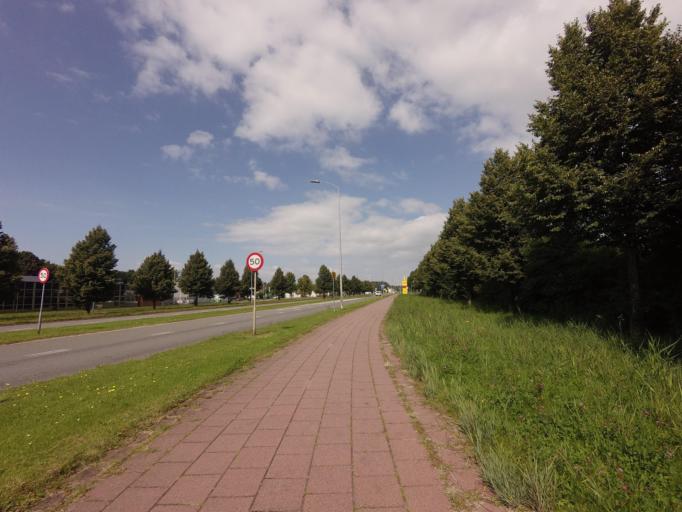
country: NL
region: Flevoland
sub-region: Gemeente Lelystad
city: Lelystad
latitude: 52.5380
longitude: 5.5207
